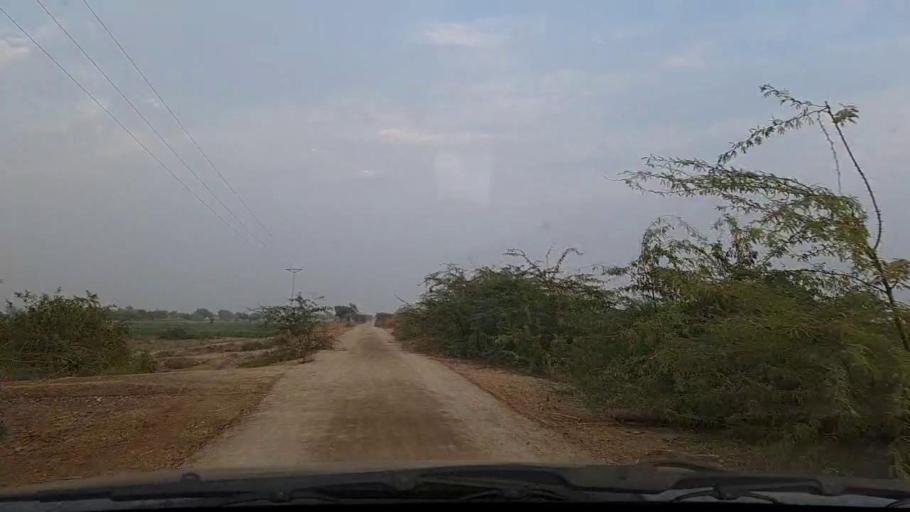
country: PK
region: Sindh
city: Dhoro Naro
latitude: 25.5932
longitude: 69.4894
